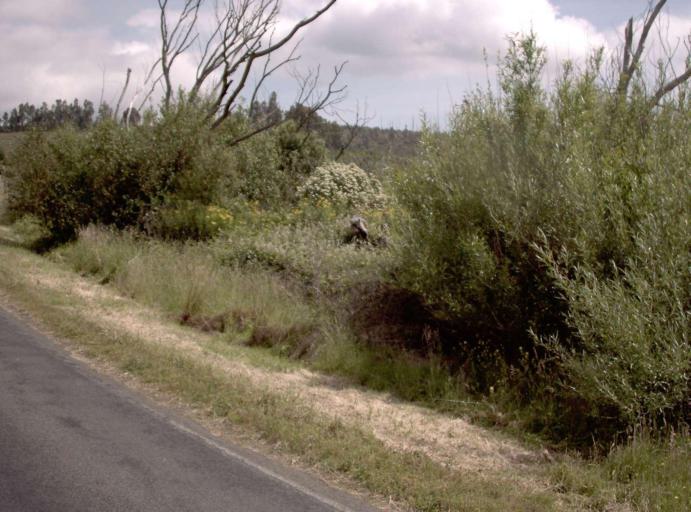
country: AU
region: Victoria
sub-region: Latrobe
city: Traralgon
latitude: -38.3547
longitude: 146.5694
